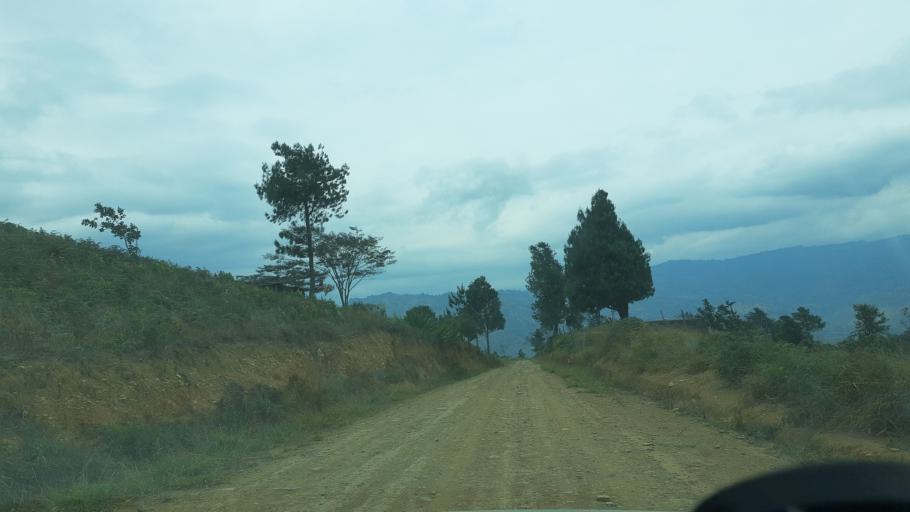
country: CO
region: Boyaca
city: Somondoco
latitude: 4.9890
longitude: -73.3755
